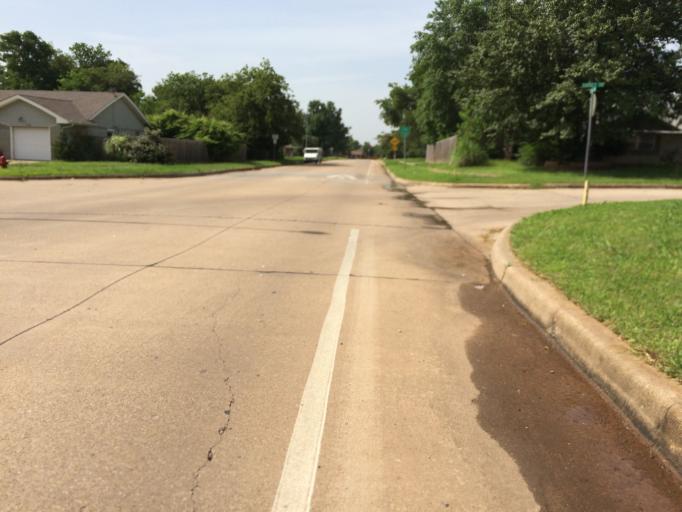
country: US
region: Oklahoma
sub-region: Cleveland County
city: Norman
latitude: 35.2142
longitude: -97.4163
